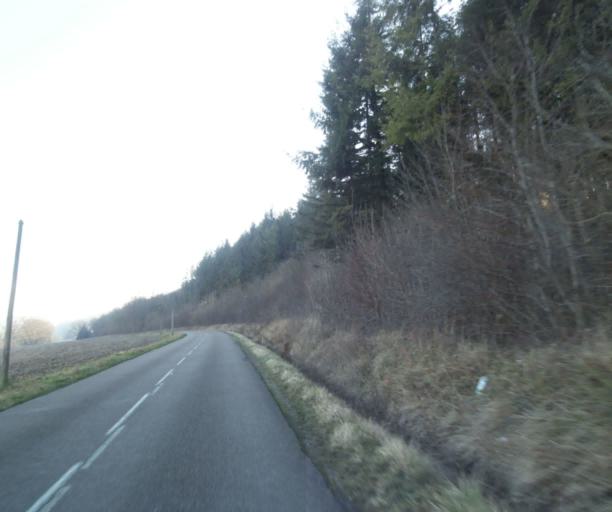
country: FR
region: Champagne-Ardenne
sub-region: Departement de la Haute-Marne
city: Bienville
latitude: 48.5613
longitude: 5.0826
